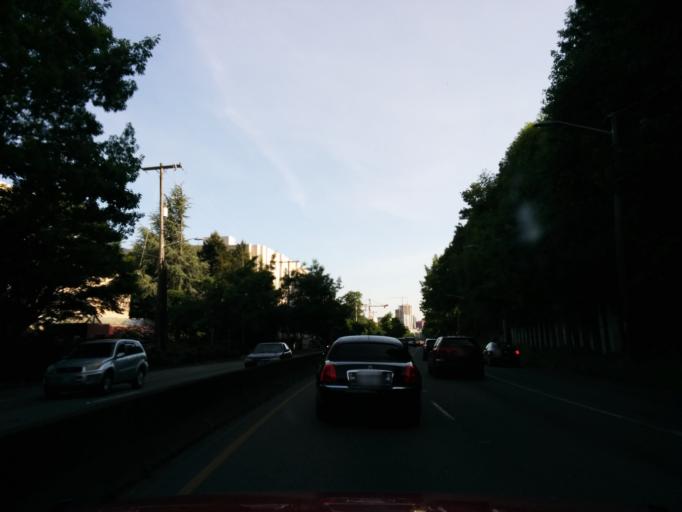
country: US
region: Washington
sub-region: King County
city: Seattle
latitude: 47.6359
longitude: -122.3436
